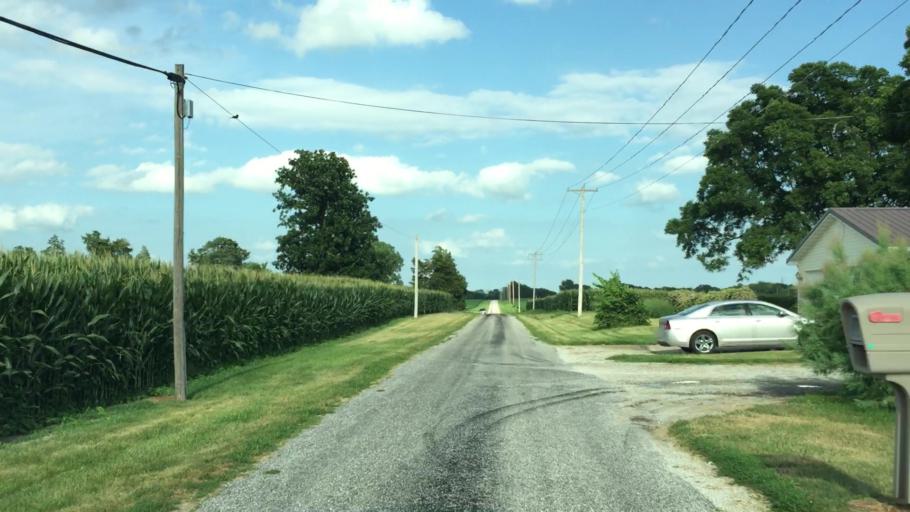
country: US
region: Illinois
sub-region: Hancock County
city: Nauvoo
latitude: 40.5495
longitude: -91.3640
